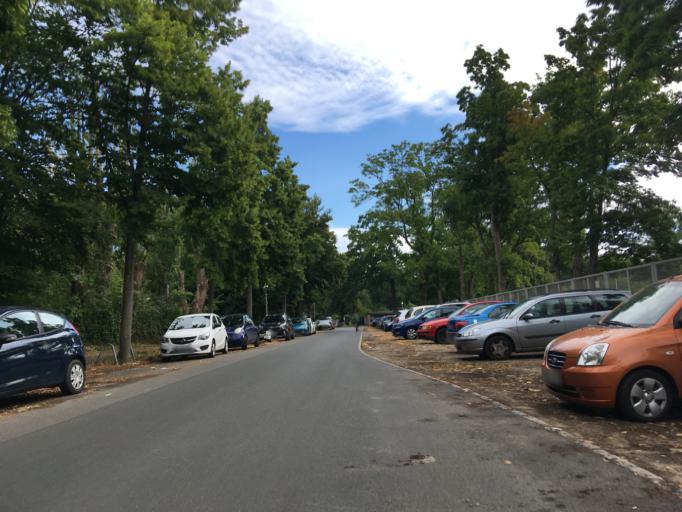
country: DE
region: Berlin
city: Hakenfelde
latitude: 52.5654
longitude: 13.2163
